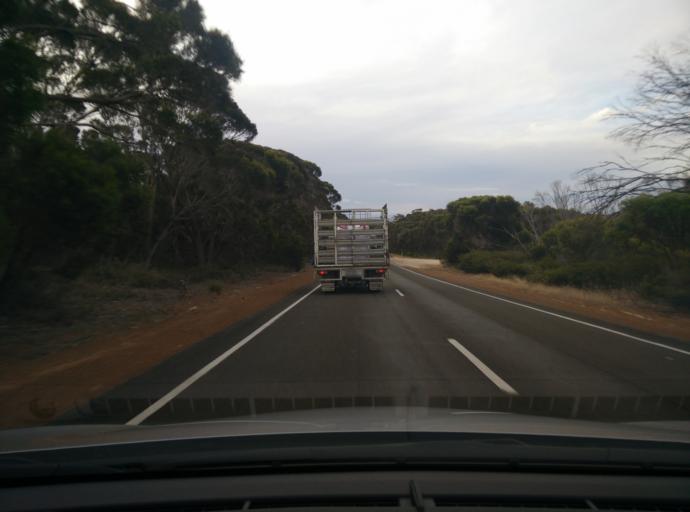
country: AU
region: South Australia
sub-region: Kangaroo Island
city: Kingscote
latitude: -35.7518
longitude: 137.5964
